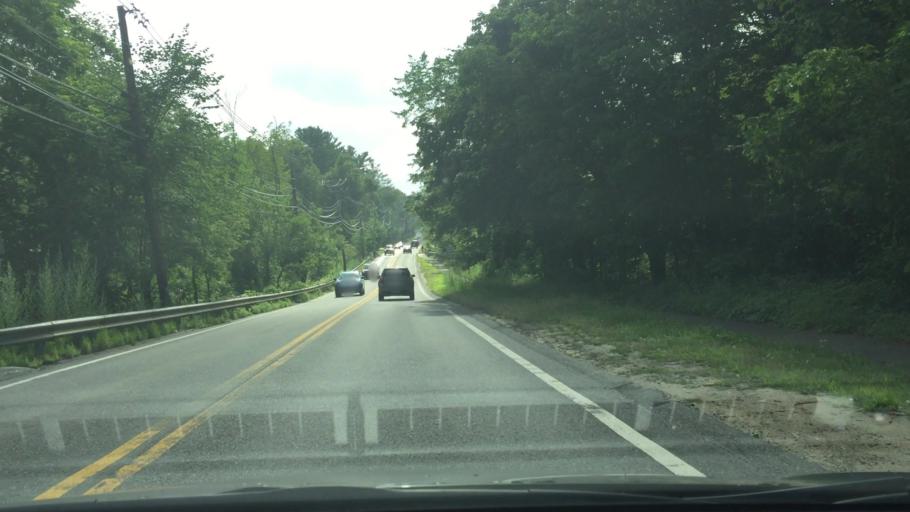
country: US
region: Massachusetts
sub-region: Middlesex County
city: Acton
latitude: 42.4760
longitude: -71.4697
